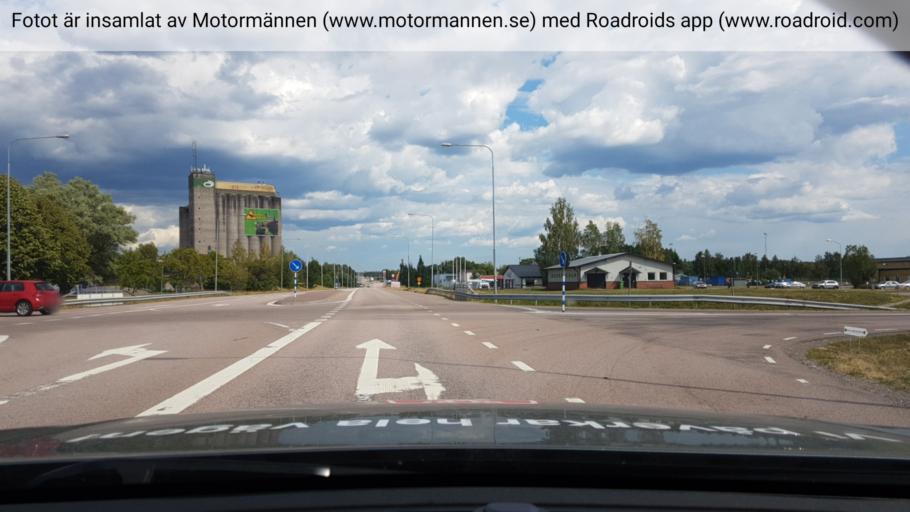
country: SE
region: Uppsala
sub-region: Heby Kommun
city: Heby
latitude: 59.9360
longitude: 16.8567
